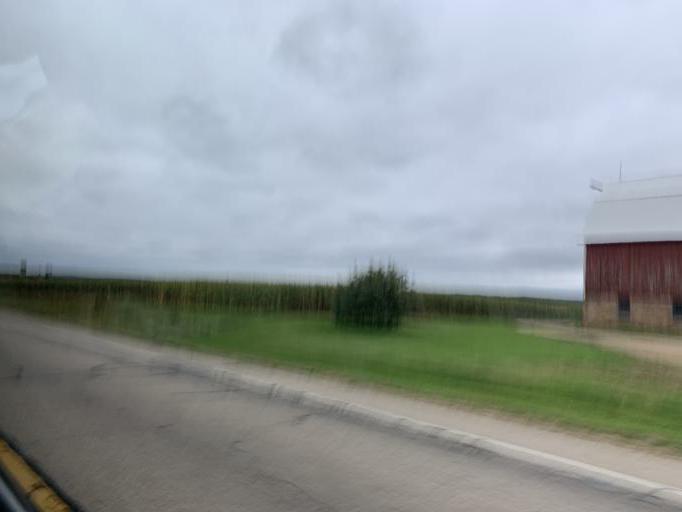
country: US
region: Wisconsin
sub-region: Grant County
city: Muscoda
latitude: 43.2198
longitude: -90.4839
